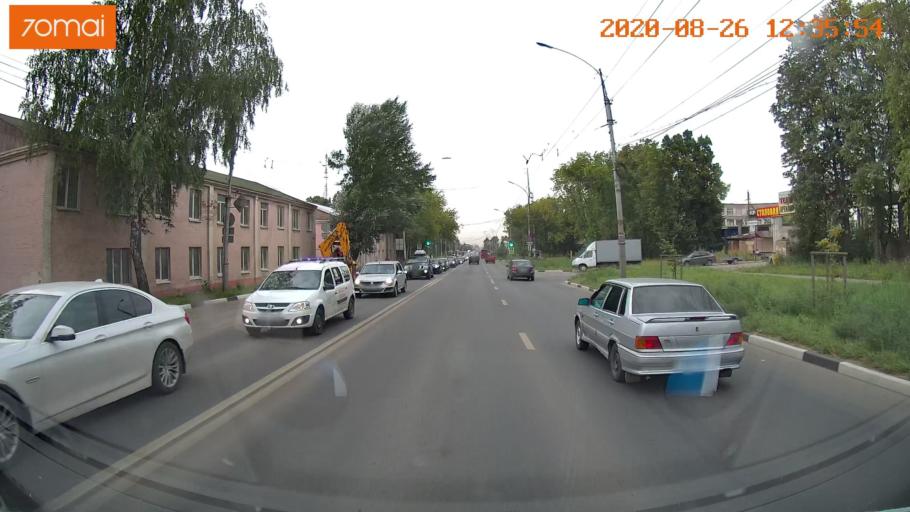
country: RU
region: Rjazan
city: Ryazan'
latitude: 54.5992
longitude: 39.7666
